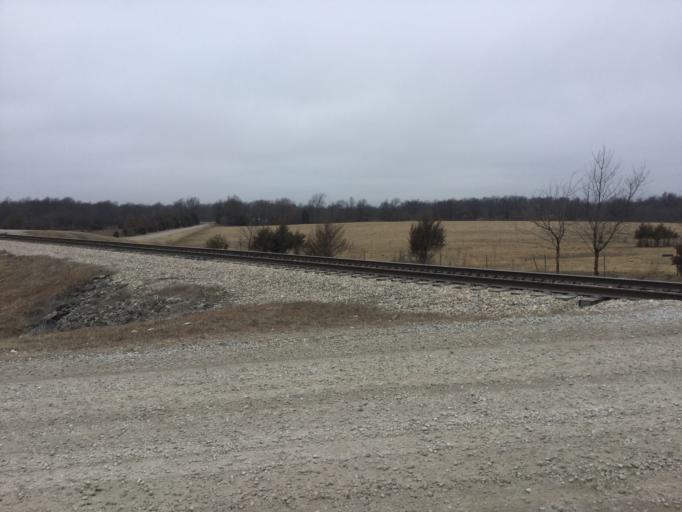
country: US
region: Kansas
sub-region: Crawford County
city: Pittsburg
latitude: 37.3603
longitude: -94.6498
